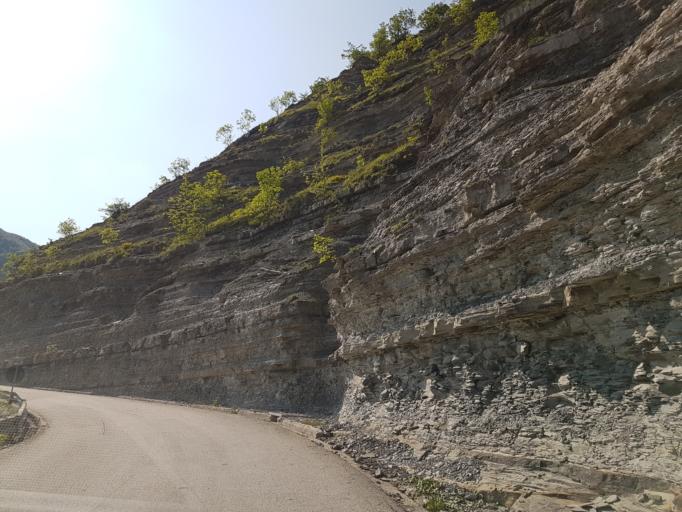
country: IT
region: Emilia-Romagna
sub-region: Forli-Cesena
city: San Piero in Bagno
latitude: 43.8116
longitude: 11.9296
